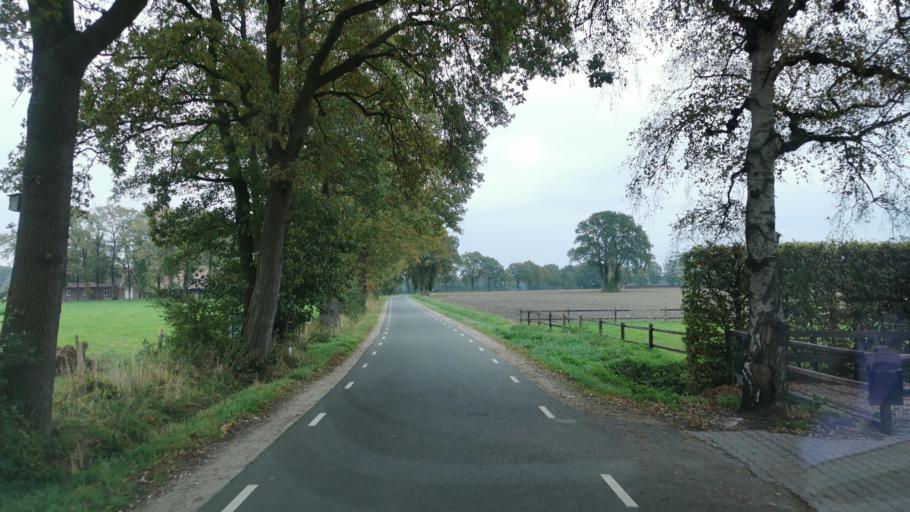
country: NL
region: Overijssel
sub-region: Gemeente Losser
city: Losser
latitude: 52.2479
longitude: 6.9939
